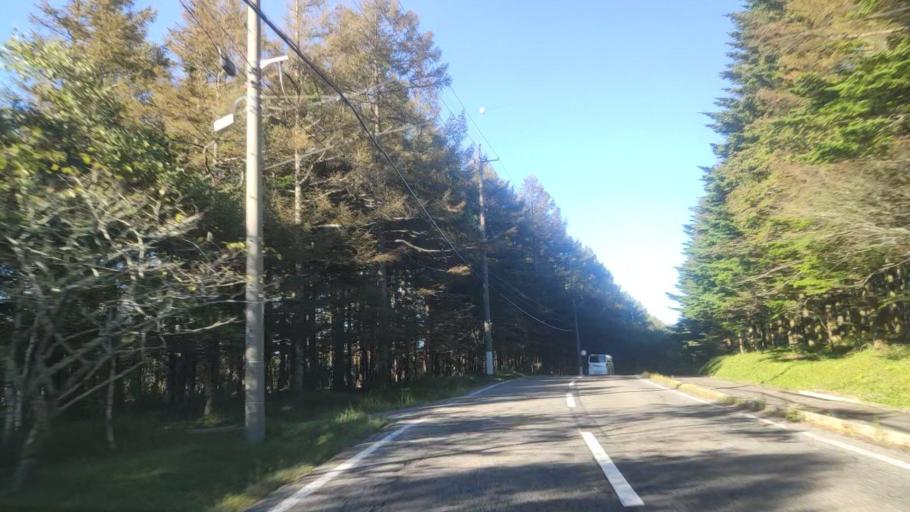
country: JP
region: Nagano
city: Kamimaruko
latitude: 36.1454
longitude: 138.2729
